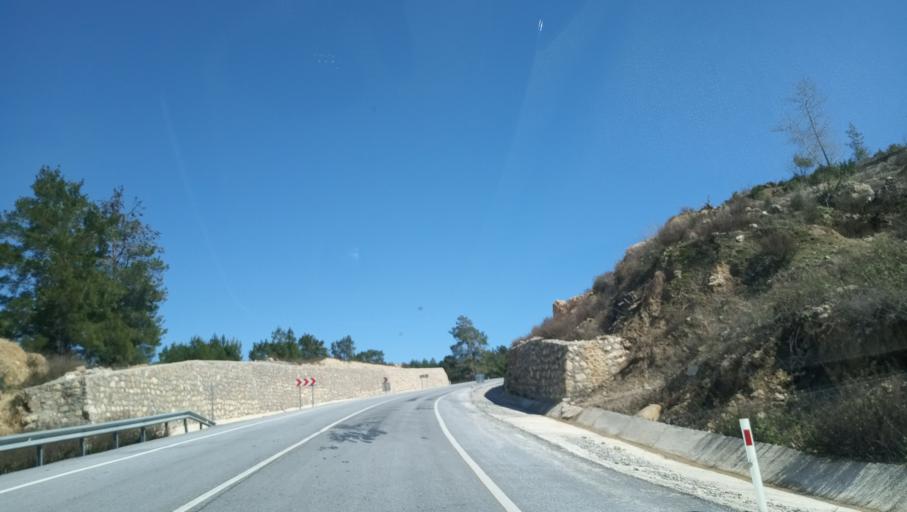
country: TR
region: Antalya
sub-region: Alanya
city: Okurcalar
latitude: 36.7752
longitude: 31.7548
